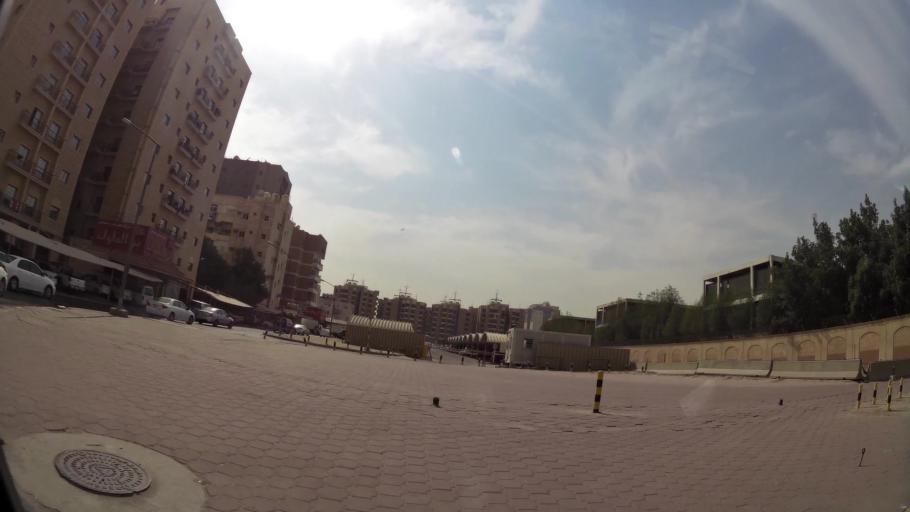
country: KW
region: Al Farwaniyah
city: Al Farwaniyah
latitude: 29.2826
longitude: 47.9720
